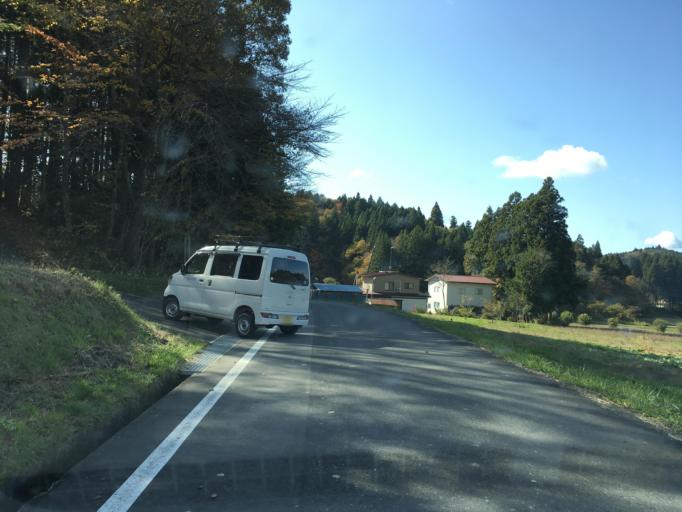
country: JP
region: Iwate
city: Ichinoseki
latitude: 38.9449
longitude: 141.4158
